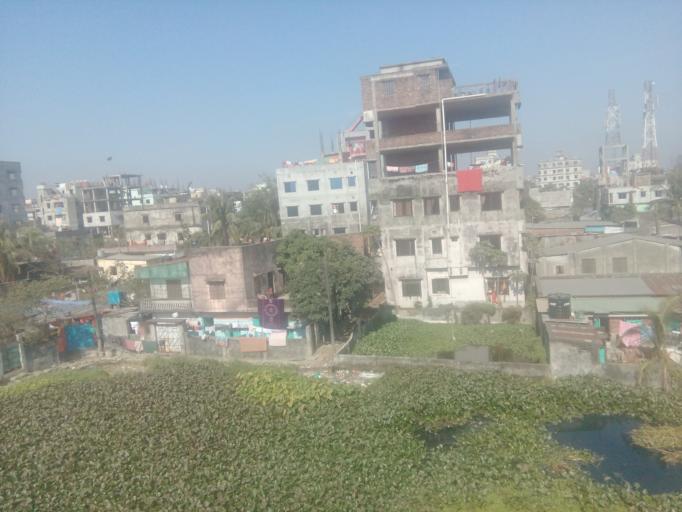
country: BD
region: Dhaka
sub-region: Dhaka
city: Dhaka
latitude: 23.7056
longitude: 90.4750
